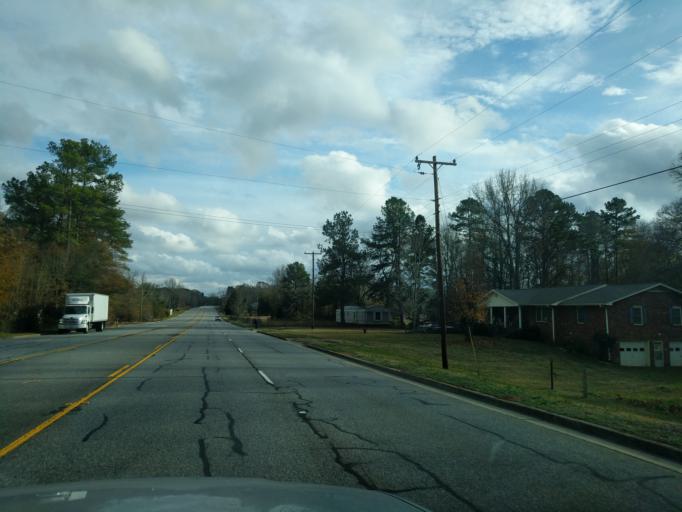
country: US
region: South Carolina
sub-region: Greenwood County
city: Ware Shoals
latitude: 34.4397
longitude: -82.2498
